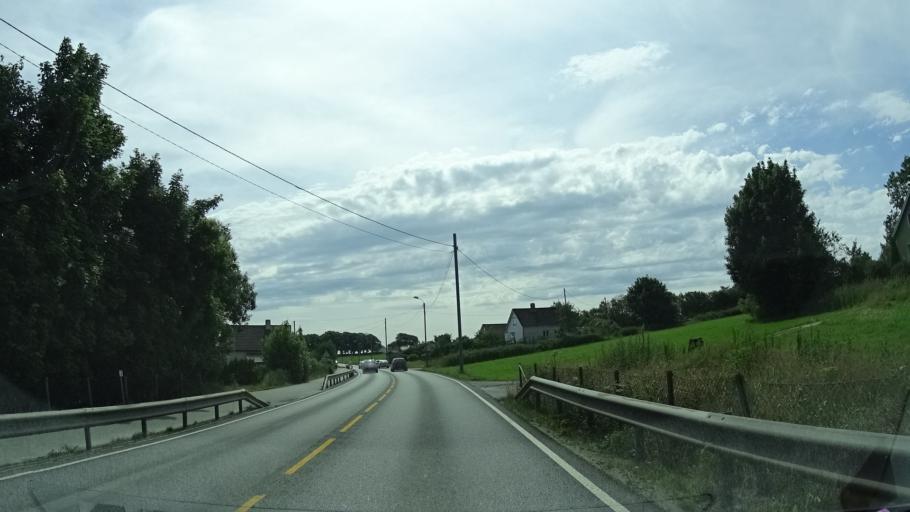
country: NO
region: Rogaland
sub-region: Randaberg
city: Randaberg
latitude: 58.9872
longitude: 5.6651
